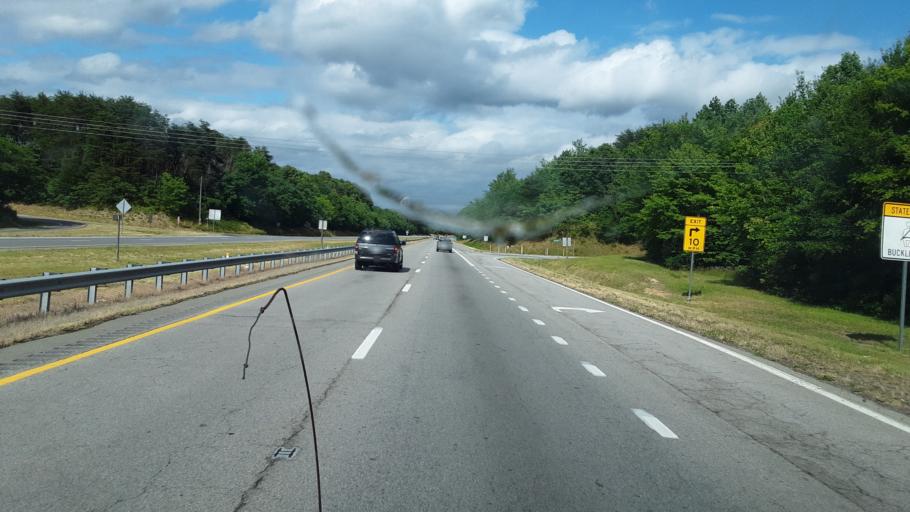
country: US
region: Virginia
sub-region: City of Danville
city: Danville
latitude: 36.5440
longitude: -79.4427
